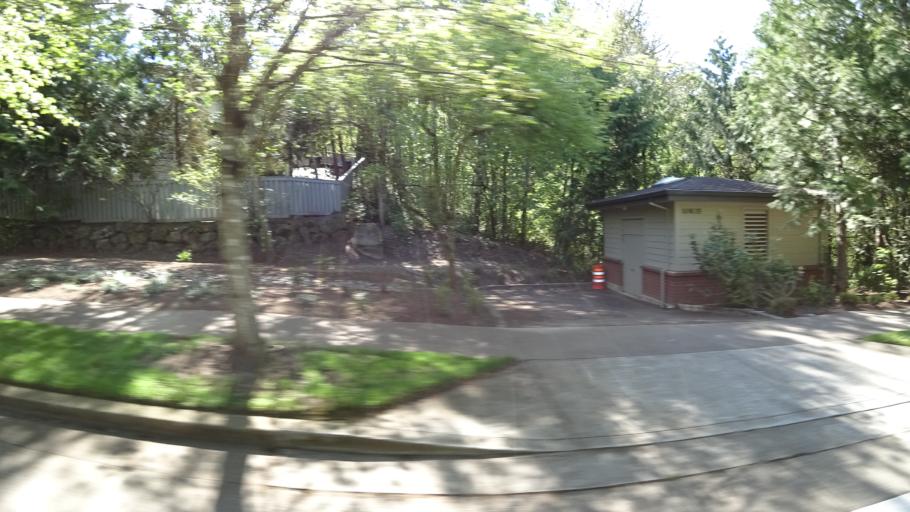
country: US
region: Oregon
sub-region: Washington County
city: King City
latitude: 45.4415
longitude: -122.8398
